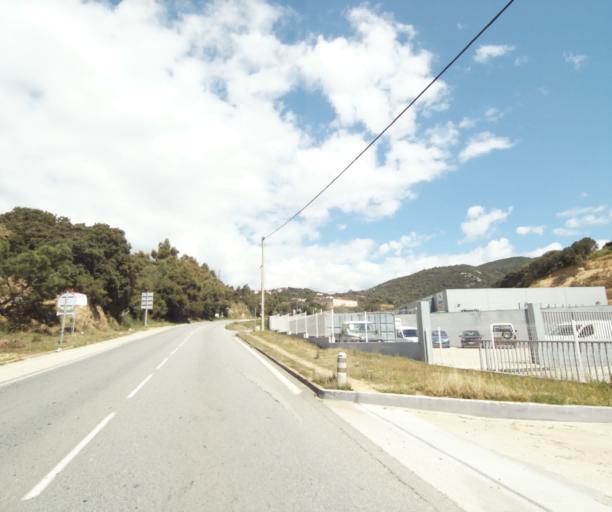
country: FR
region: Corsica
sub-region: Departement de la Corse-du-Sud
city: Propriano
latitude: 41.6646
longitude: 8.9190
